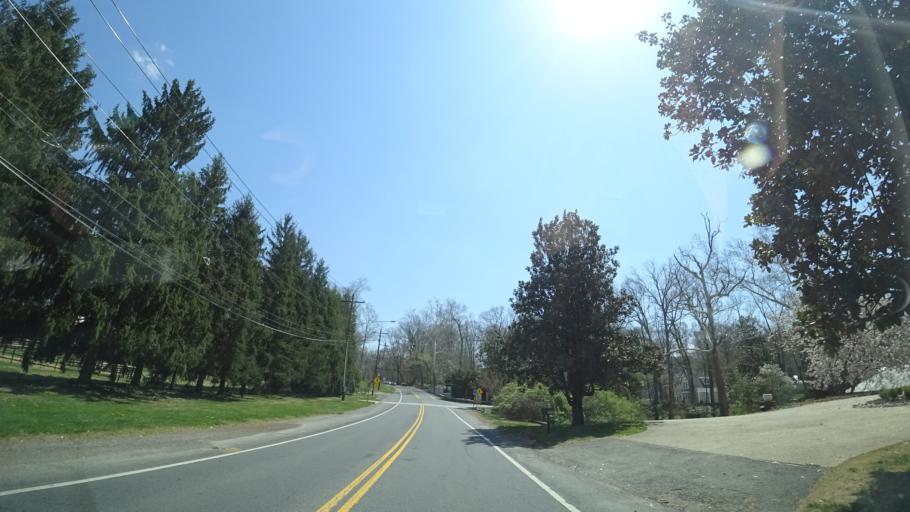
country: US
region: Maryland
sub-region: Montgomery County
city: Cabin John
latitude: 38.9986
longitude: -77.1315
